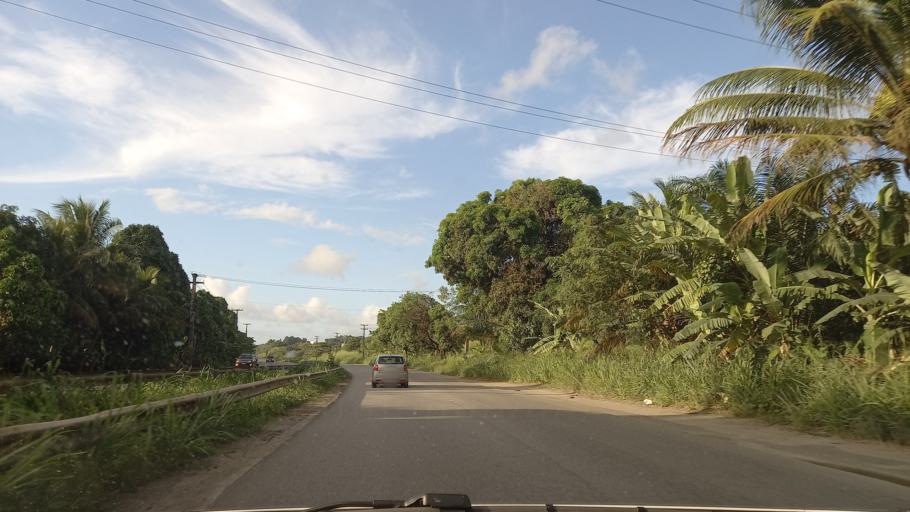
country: BR
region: Pernambuco
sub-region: Cabo De Santo Agostinho
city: Cabo
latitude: -8.3331
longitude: -35.0108
